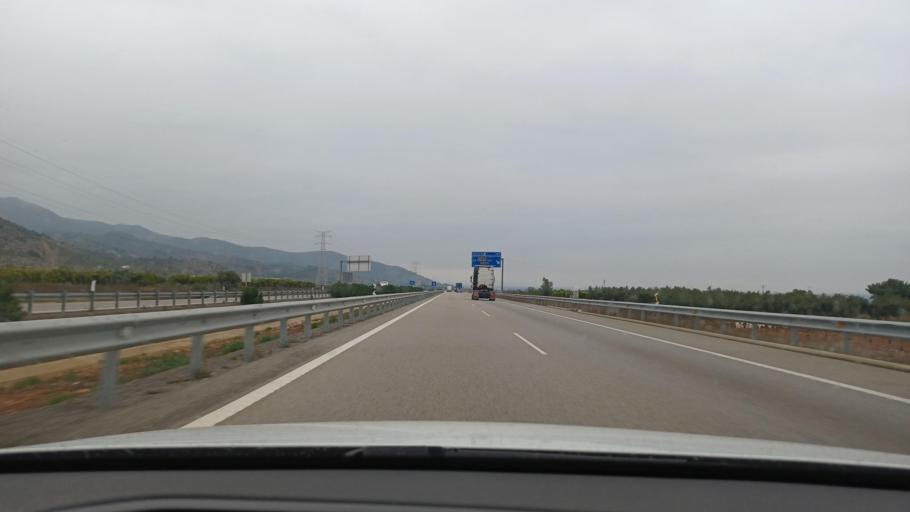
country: ES
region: Valencia
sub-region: Provincia de Castello
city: Villavieja
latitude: 39.8212
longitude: -0.2088
